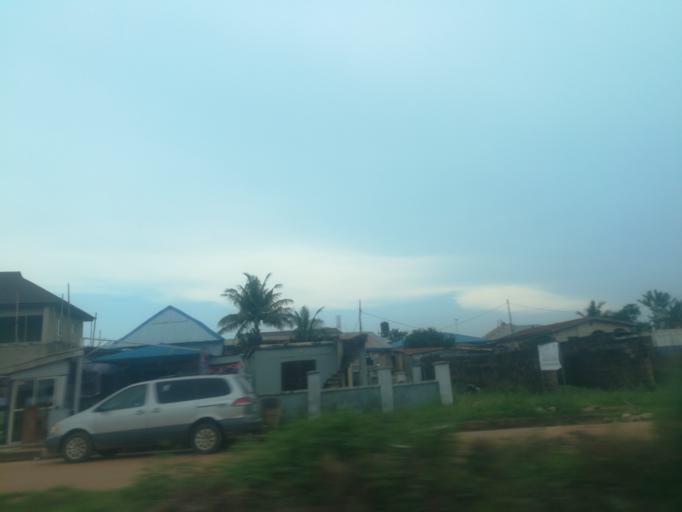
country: NG
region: Oyo
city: Ibadan
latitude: 7.3667
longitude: 3.8119
